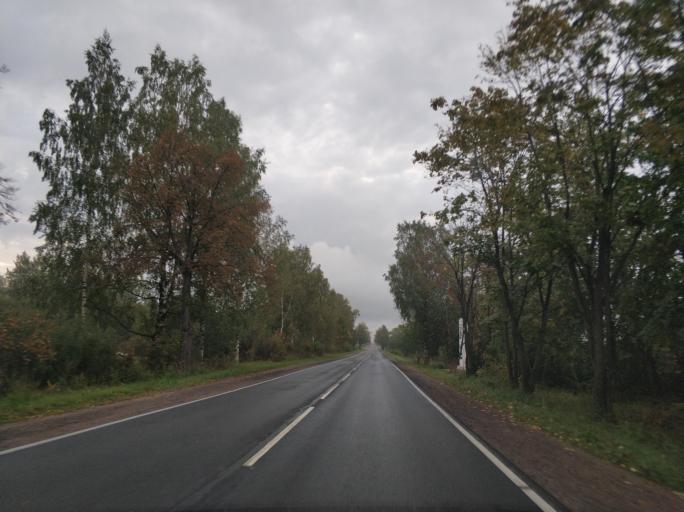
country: RU
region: Leningrad
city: Borisova Griva
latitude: 60.0836
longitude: 30.8983
